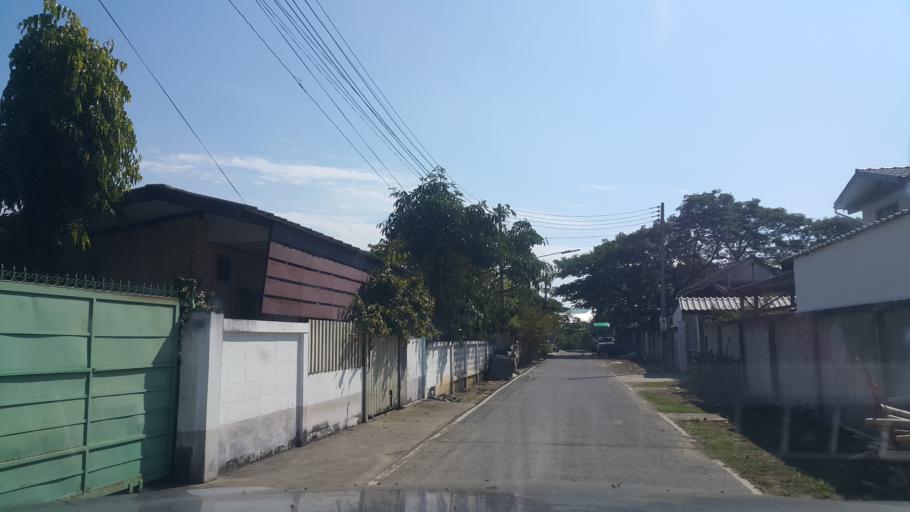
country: TH
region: Chiang Mai
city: Chiang Mai
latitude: 18.7750
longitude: 99.0363
